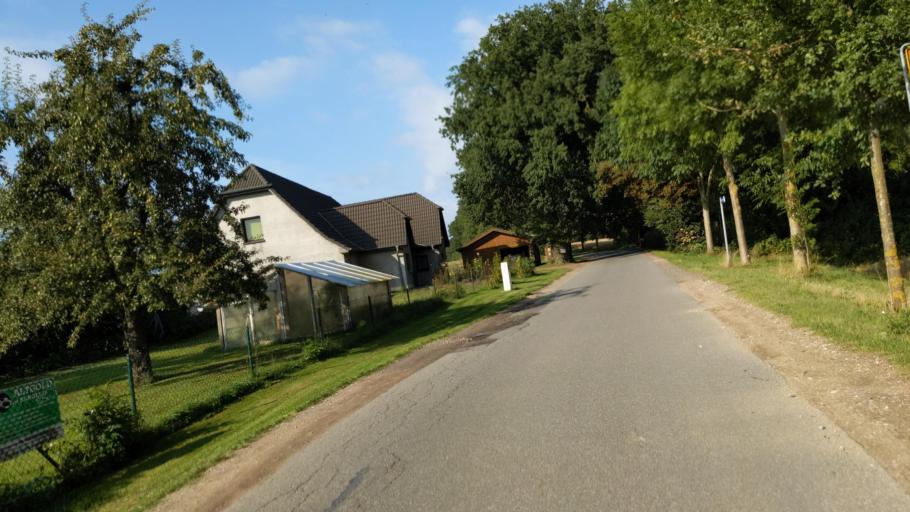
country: DE
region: Mecklenburg-Vorpommern
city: Kalkhorst
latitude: 53.9646
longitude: 11.0086
